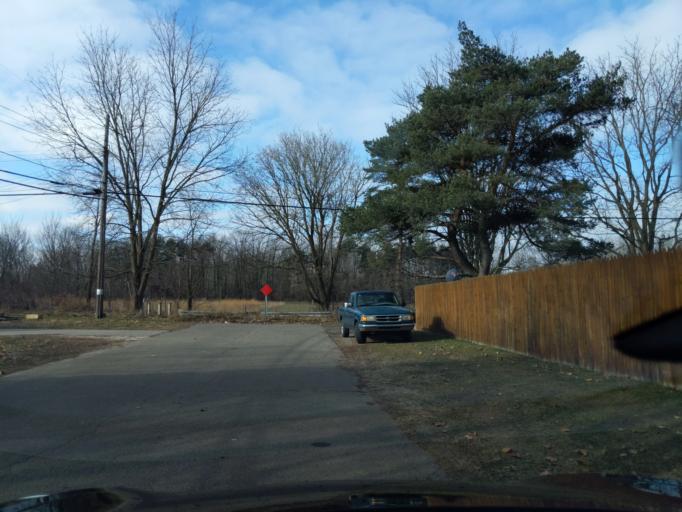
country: US
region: Michigan
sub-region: Ingham County
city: Lansing
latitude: 42.6948
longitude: -84.5720
